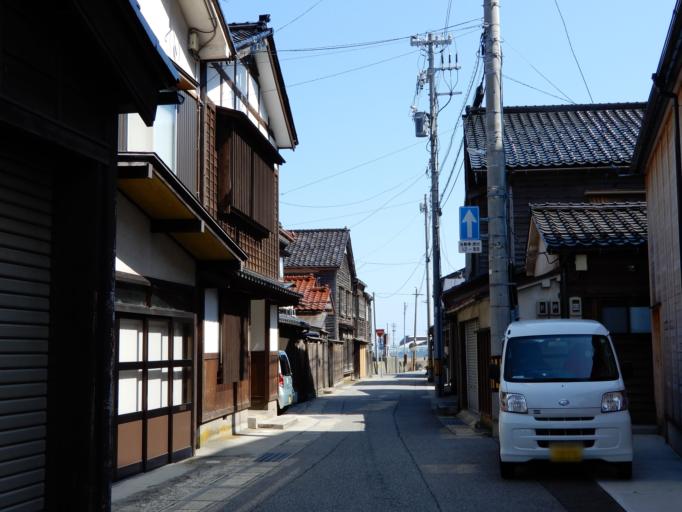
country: JP
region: Ishikawa
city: Nanao
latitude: 37.3971
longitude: 136.9006
